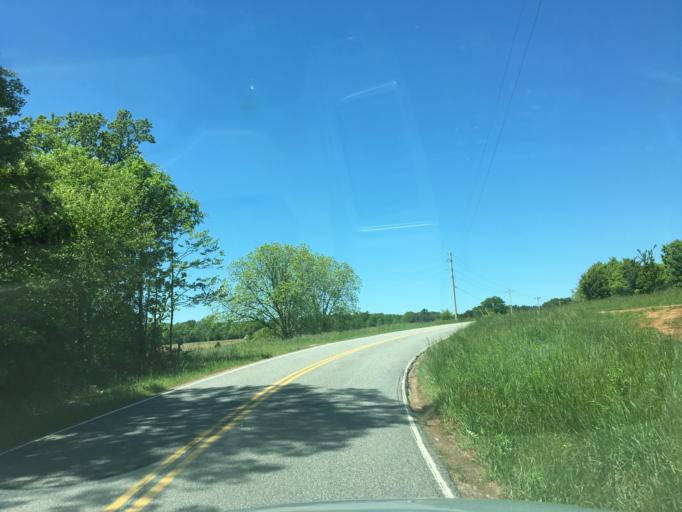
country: US
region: South Carolina
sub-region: Spartanburg County
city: Duncan
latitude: 34.8722
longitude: -82.1779
